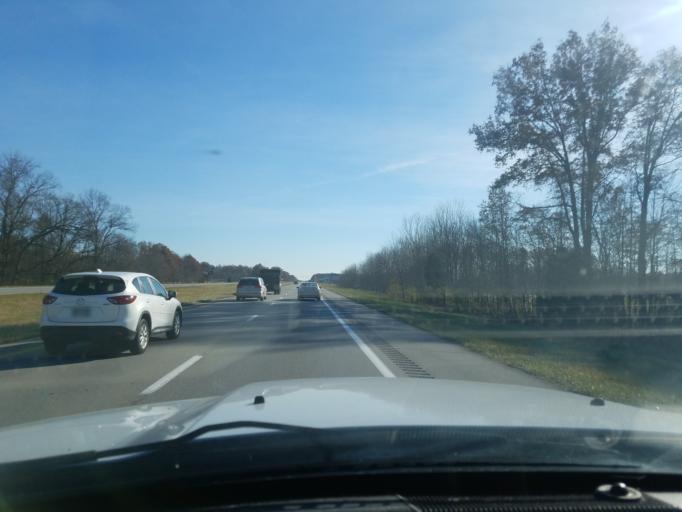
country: US
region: Ohio
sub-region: Clermont County
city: Williamsburg
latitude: 39.0576
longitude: -83.9899
